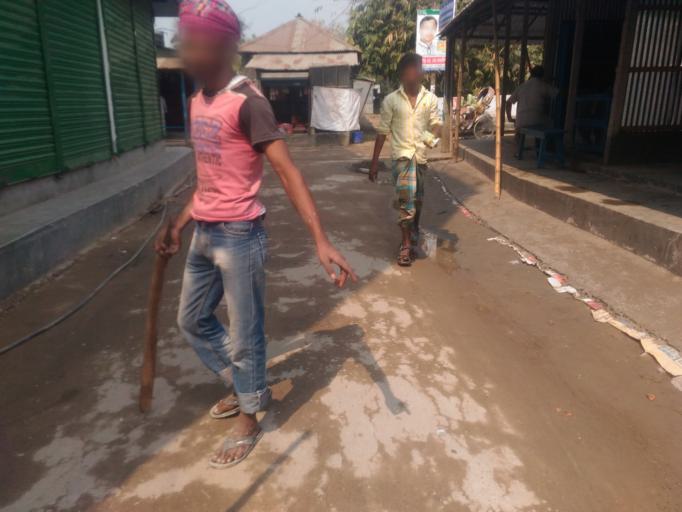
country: BD
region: Dhaka
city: Tungi
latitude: 23.9935
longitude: 90.3771
